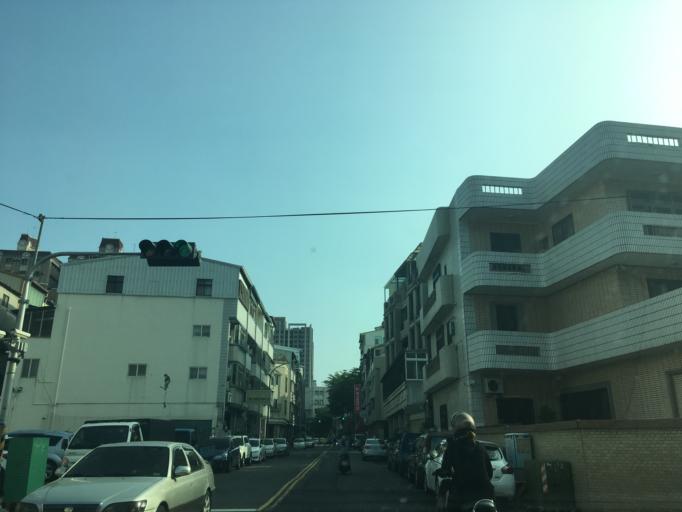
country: TW
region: Taiwan
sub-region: Taichung City
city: Taichung
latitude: 24.1684
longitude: 120.6801
